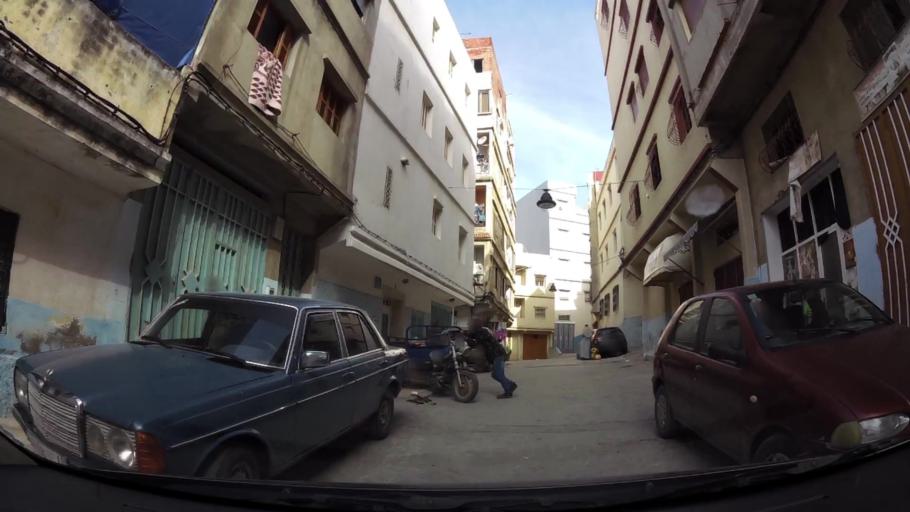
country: MA
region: Tanger-Tetouan
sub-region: Tanger-Assilah
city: Tangier
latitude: 35.7692
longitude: -5.7685
